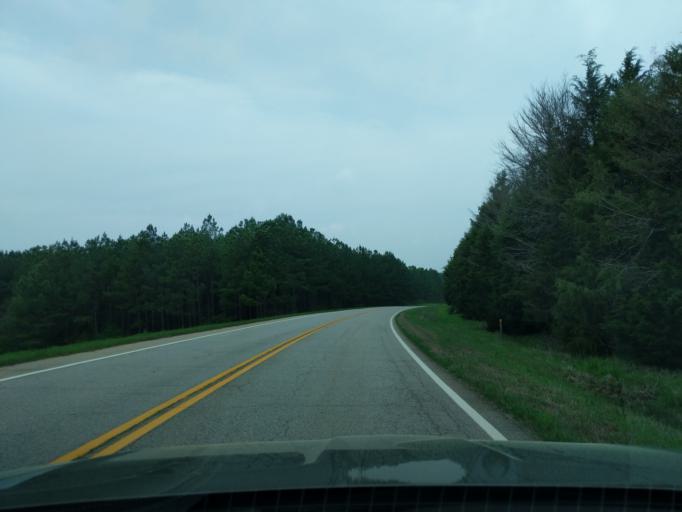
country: US
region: Georgia
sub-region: Lincoln County
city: Lincolnton
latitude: 33.7933
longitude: -82.3840
